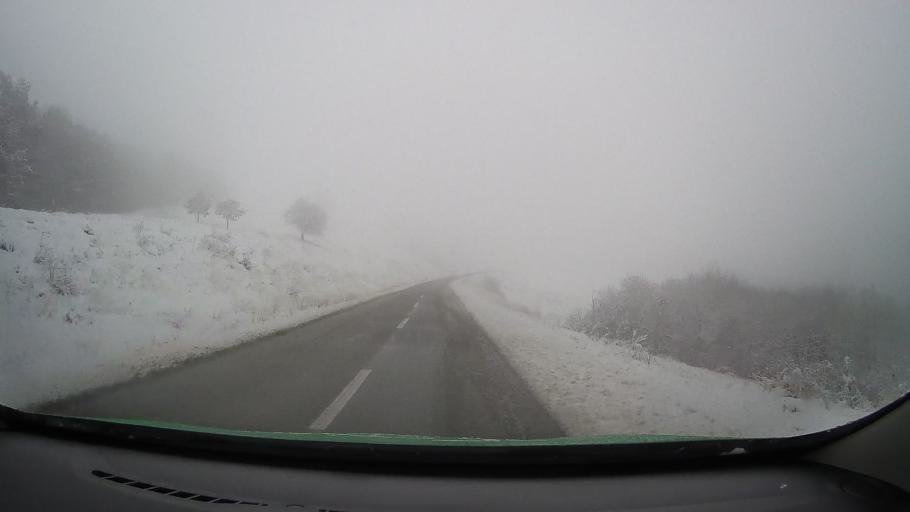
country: RO
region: Hunedoara
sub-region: Comuna Teliucu Inferior
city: Teliucu Inferior
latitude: 45.6684
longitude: 22.9178
